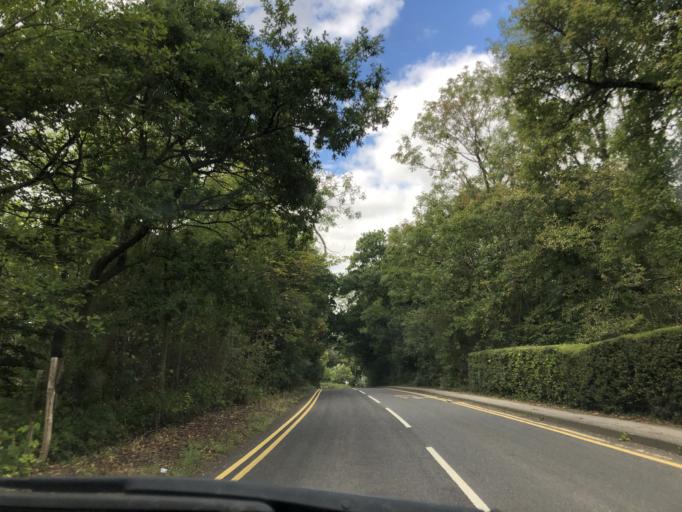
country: GB
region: England
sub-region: Kent
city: Tonbridge
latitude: 51.2158
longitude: 0.2263
